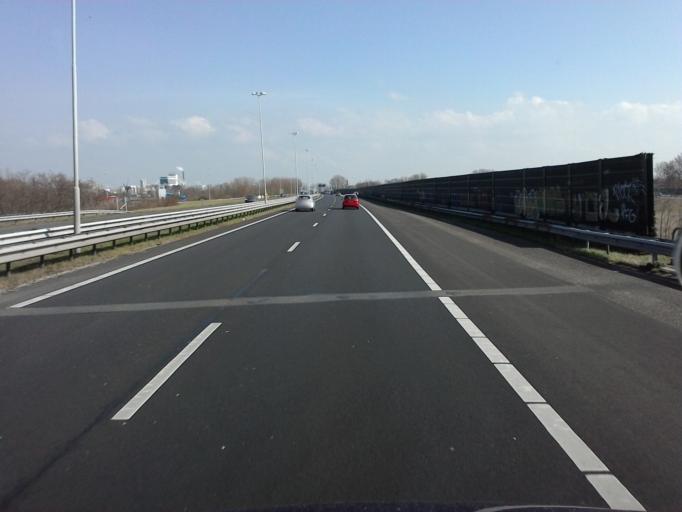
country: NL
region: North Holland
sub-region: Gemeente Zaanstad
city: Zaanstad
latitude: 52.4665
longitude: 4.7970
